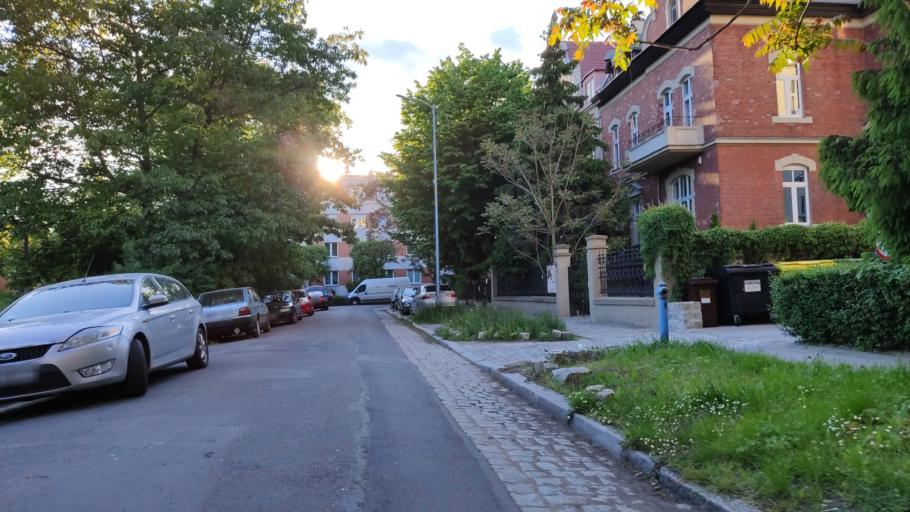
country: PL
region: Lower Silesian Voivodeship
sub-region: Powiat wroclawski
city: Wroclaw
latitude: 51.0852
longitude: 17.0070
